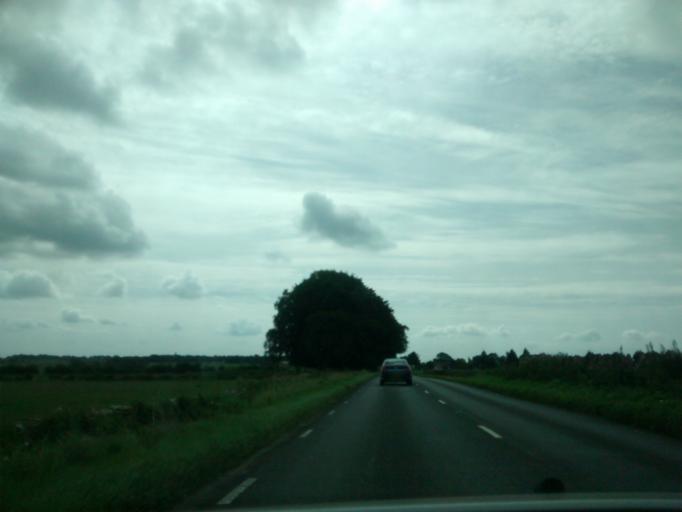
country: GB
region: England
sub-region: South Gloucestershire
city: Cold Ashton
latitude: 51.4230
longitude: -2.3995
